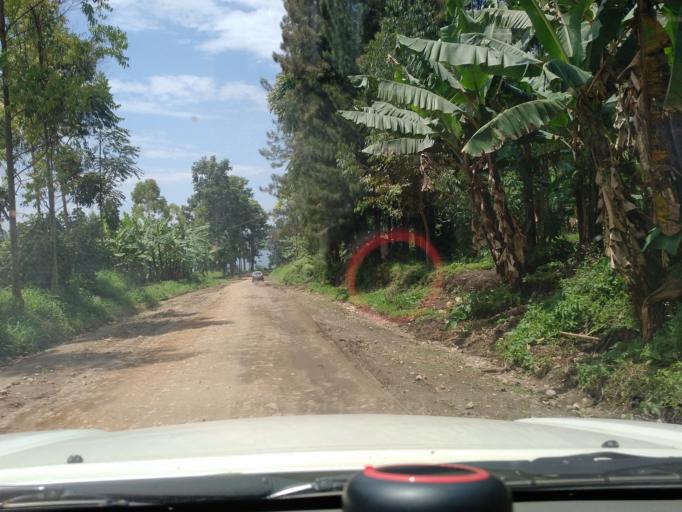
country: CD
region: Nord Kivu
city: Sake
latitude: -1.6162
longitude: 29.0236
